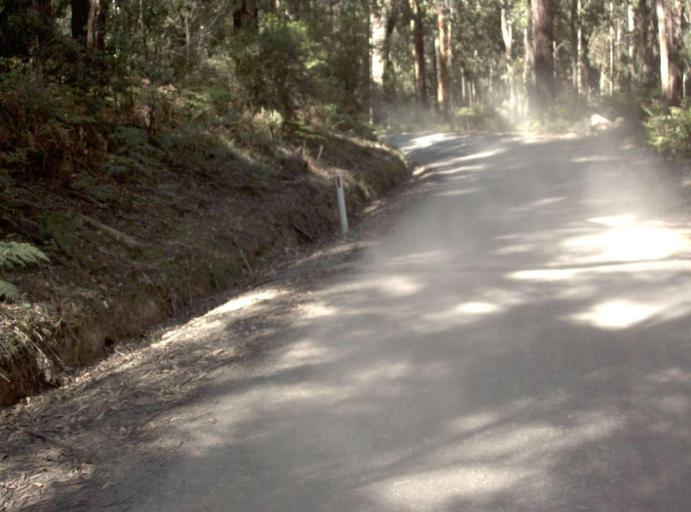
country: AU
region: New South Wales
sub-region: Bombala
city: Bombala
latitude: -37.2459
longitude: 148.7526
